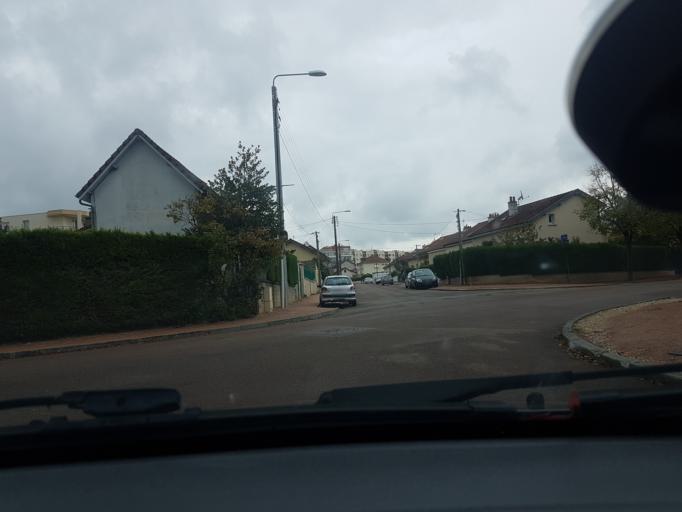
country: FR
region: Bourgogne
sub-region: Departement de la Cote-d'Or
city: Longvic
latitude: 47.3114
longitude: 5.0552
